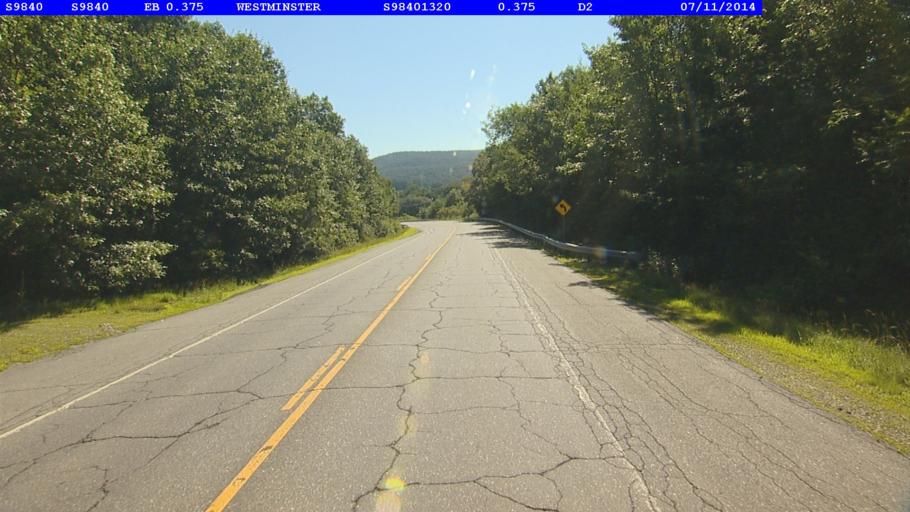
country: US
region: Vermont
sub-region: Windham County
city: Bellows Falls
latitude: 43.0913
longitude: -72.4496
